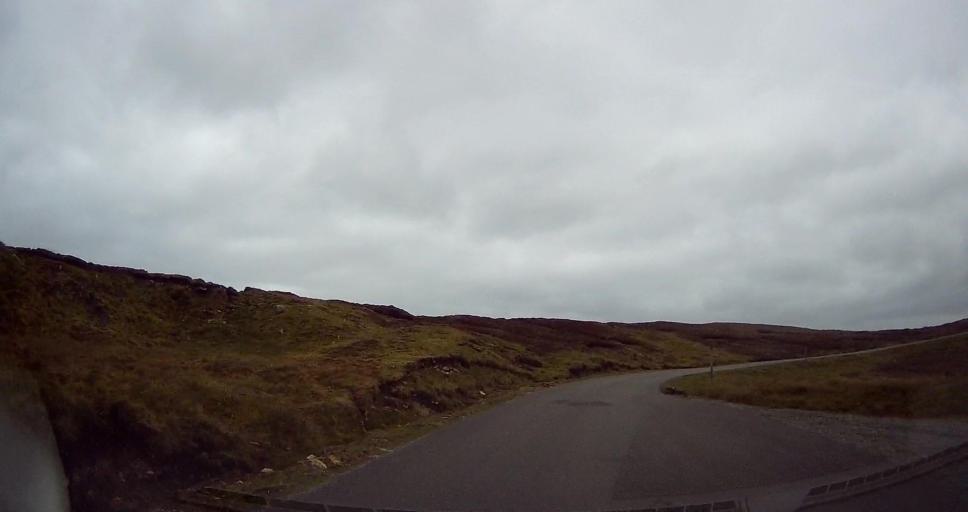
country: GB
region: Scotland
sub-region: Shetland Islands
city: Lerwick
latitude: 60.3183
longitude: -1.3419
